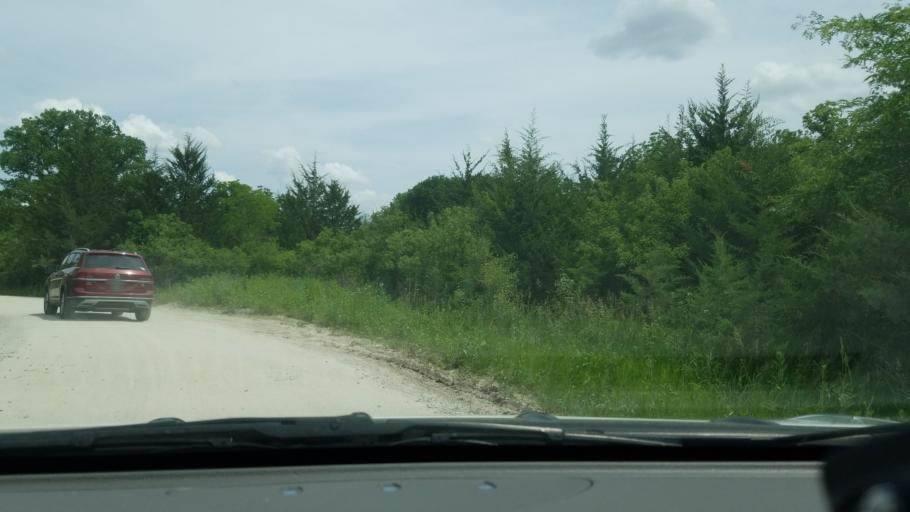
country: US
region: Nebraska
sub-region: Saunders County
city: Ashland
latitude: 41.0147
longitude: -96.2946
